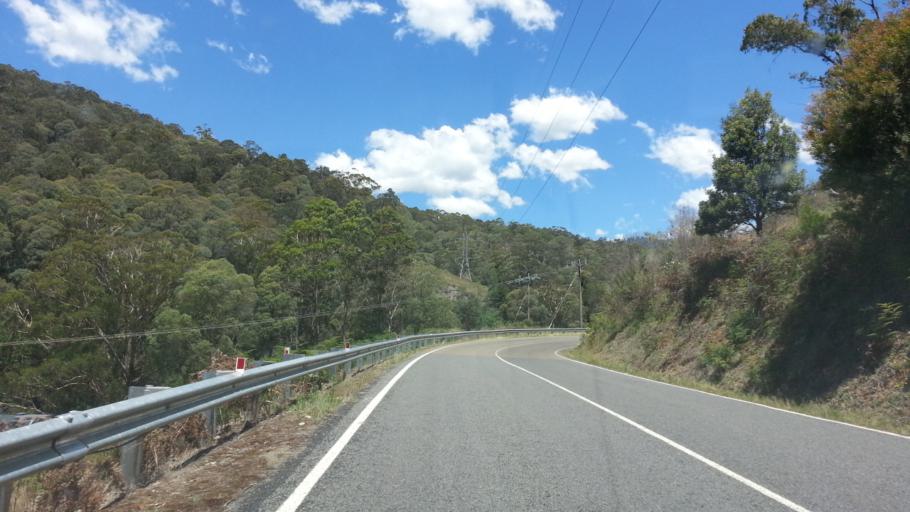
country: AU
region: Victoria
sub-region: Alpine
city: Mount Beauty
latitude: -36.7853
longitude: 147.2185
